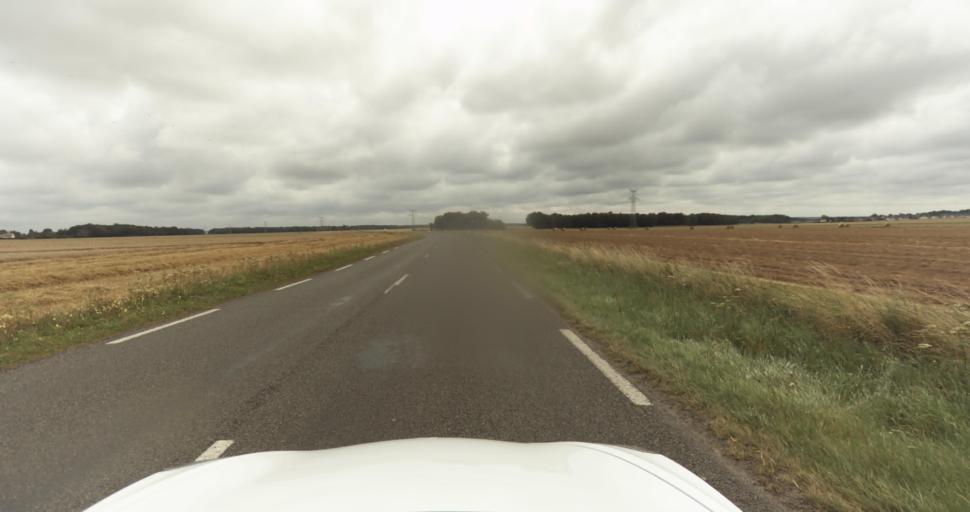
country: FR
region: Haute-Normandie
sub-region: Departement de l'Eure
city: Claville
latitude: 49.0387
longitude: 1.0298
